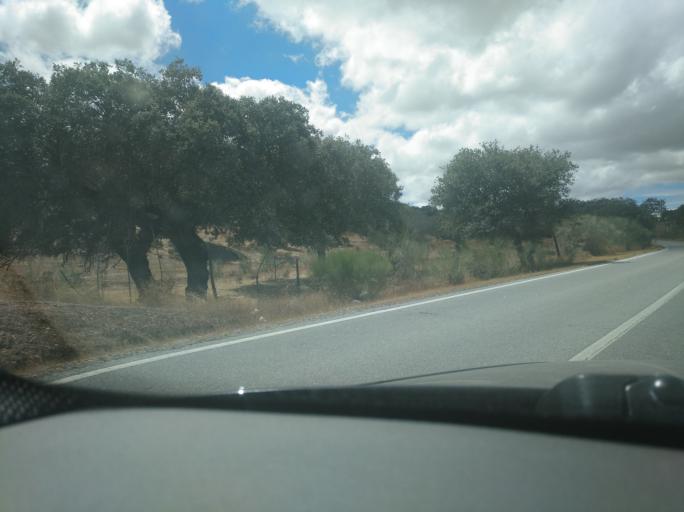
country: PT
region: Portalegre
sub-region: Campo Maior
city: Campo Maior
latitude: 38.9978
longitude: -7.1732
